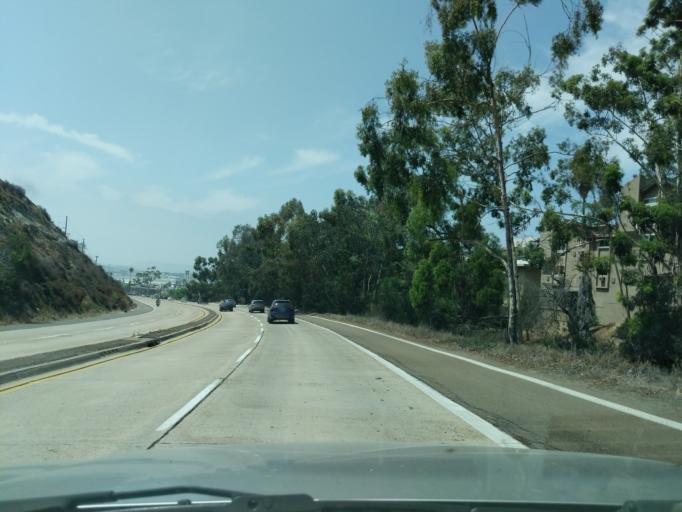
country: US
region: California
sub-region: San Diego County
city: San Diego
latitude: 32.7463
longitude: -117.1789
